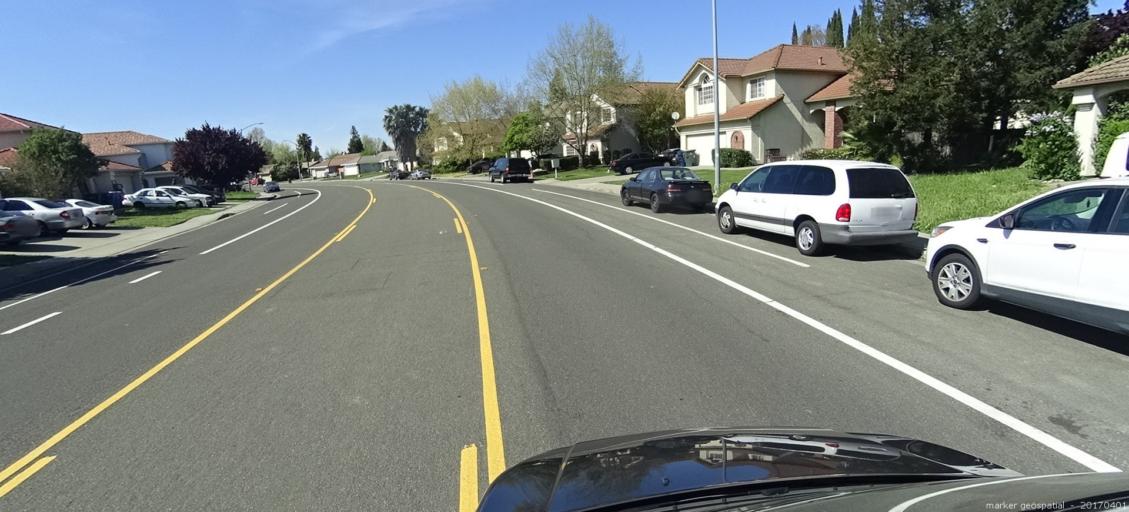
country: US
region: California
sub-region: Sacramento County
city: Laguna
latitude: 38.4450
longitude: -121.4379
